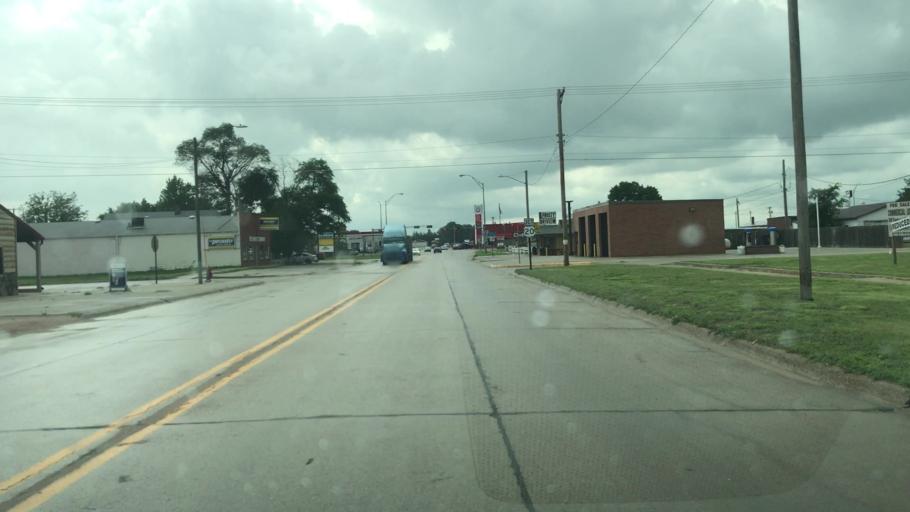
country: US
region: Nebraska
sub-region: Cherry County
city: Valentine
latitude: 42.8698
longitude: -100.5505
